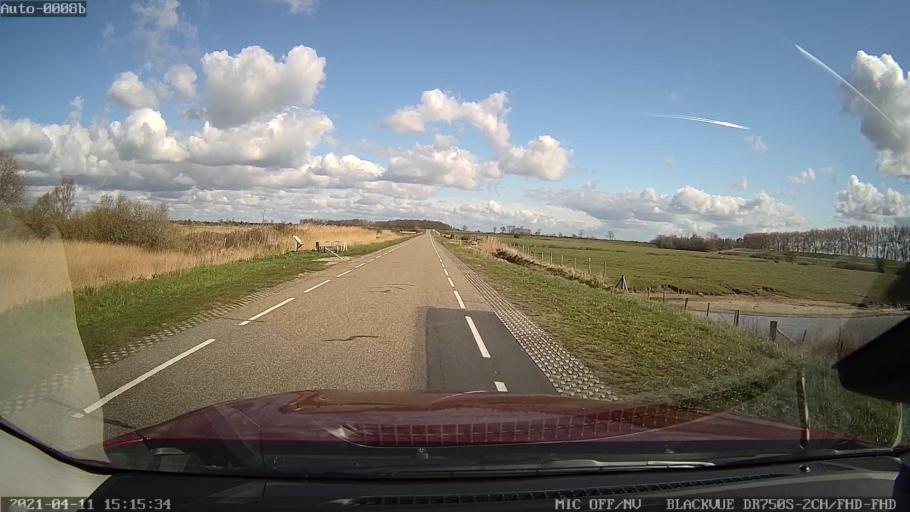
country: NL
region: Zeeland
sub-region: Schouwen-Duiveland
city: Bruinisse
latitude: 51.6798
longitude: 4.0176
